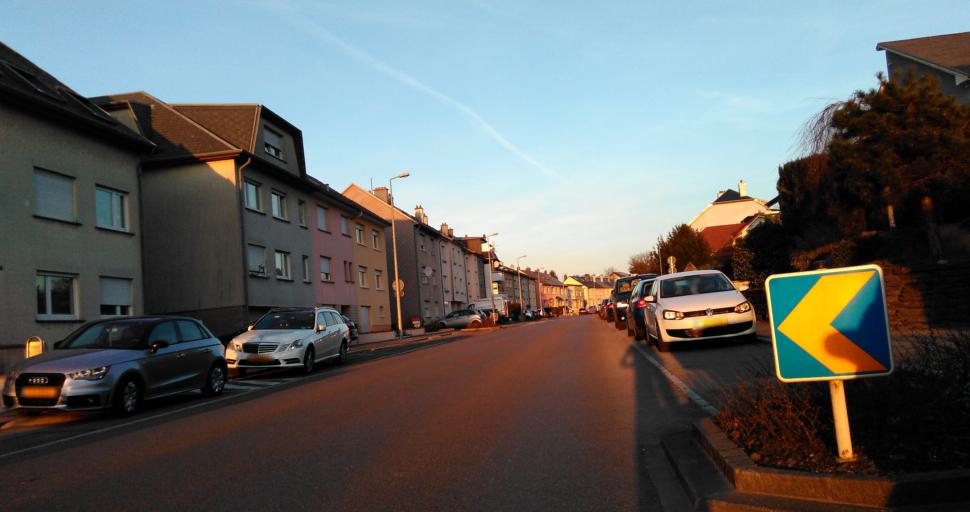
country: LU
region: Luxembourg
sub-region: Canton d'Esch-sur-Alzette
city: Petange
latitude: 49.5532
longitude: 5.8802
